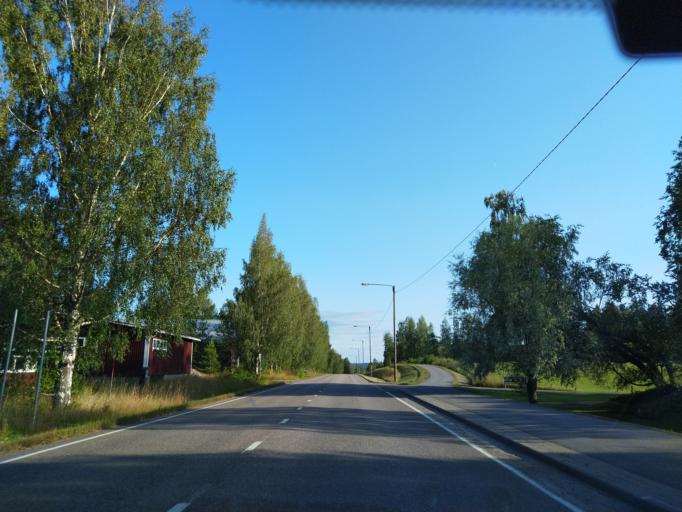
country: FI
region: Central Finland
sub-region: Jaemsae
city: Kuhmoinen
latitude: 61.5799
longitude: 25.1741
